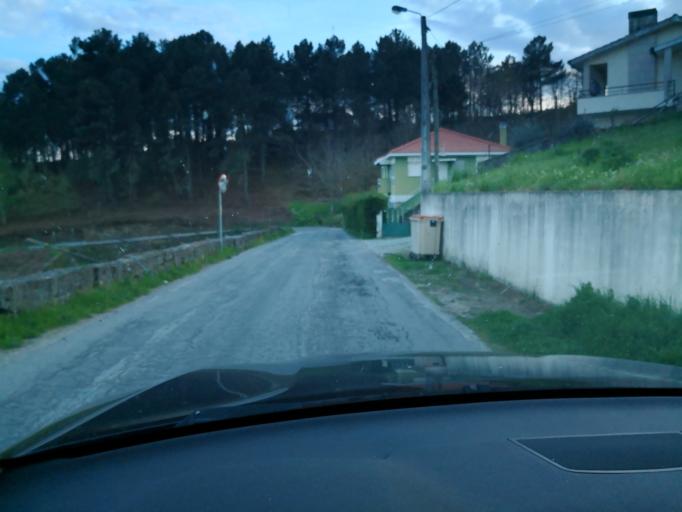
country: PT
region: Vila Real
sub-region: Vila Real
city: Vila Real
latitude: 41.3035
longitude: -7.7794
